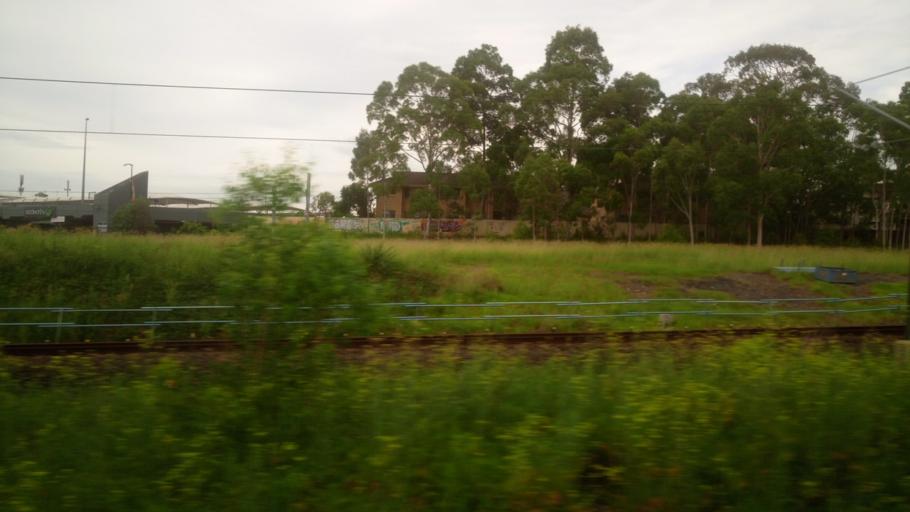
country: AU
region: New South Wales
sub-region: Blacktown
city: Blacktown
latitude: -33.7743
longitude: 150.9303
